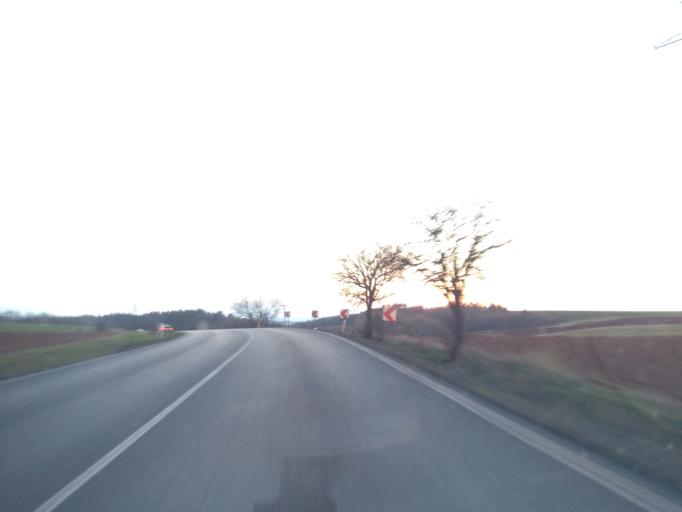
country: CZ
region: Ustecky
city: Mecholupy
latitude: 50.1608
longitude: 13.5697
